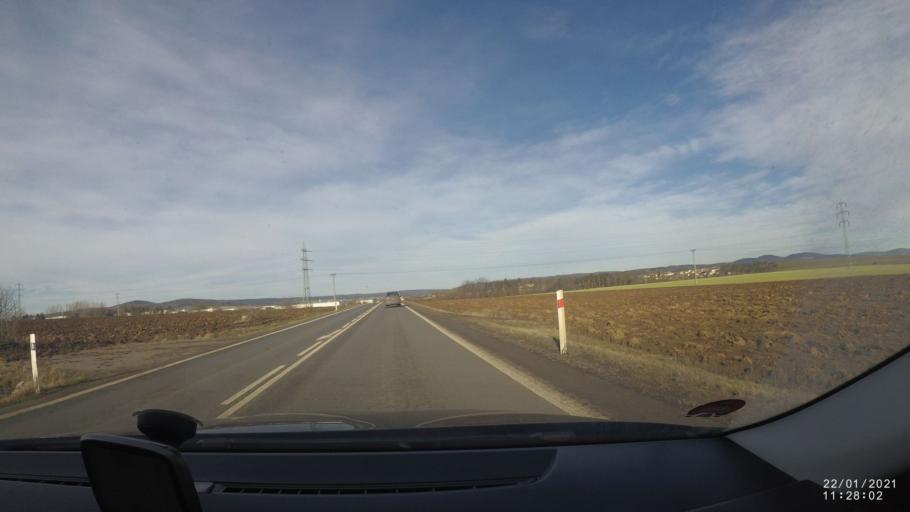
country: CZ
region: Central Bohemia
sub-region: Okres Beroun
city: Horovice
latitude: 49.8561
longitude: 13.9059
